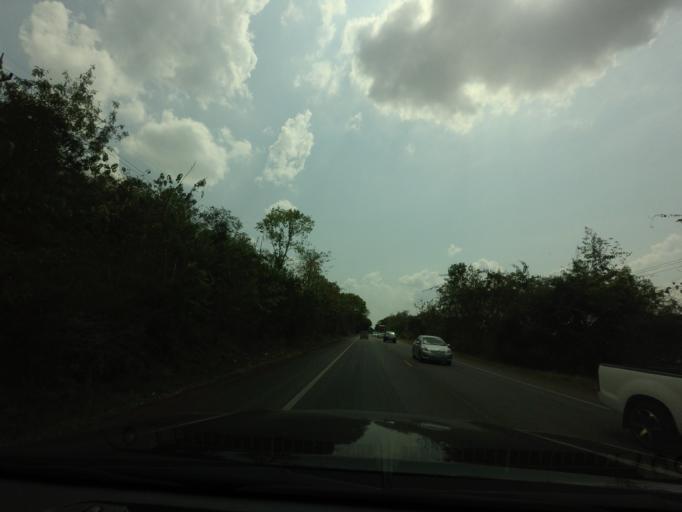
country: TH
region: Kanchanaburi
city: Sai Yok
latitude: 14.1520
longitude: 99.1422
